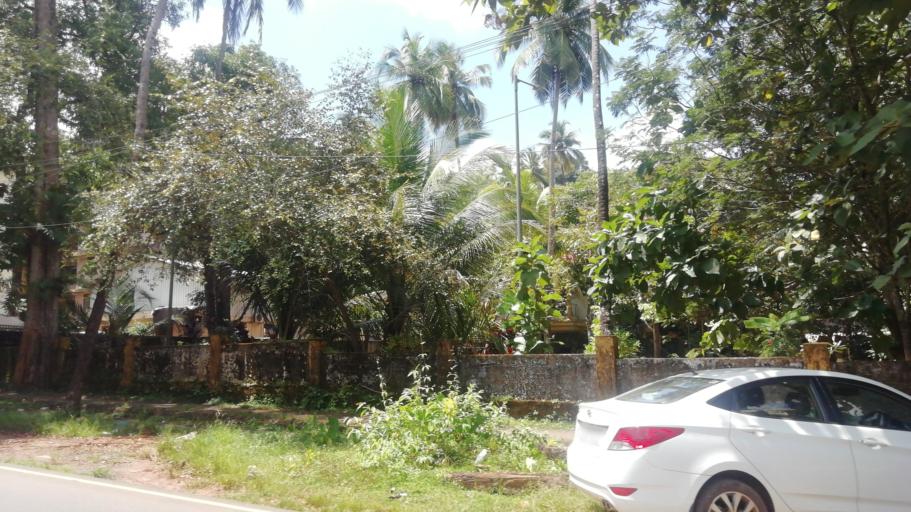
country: IN
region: Goa
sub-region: North Goa
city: Ponda
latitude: 15.3906
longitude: 74.0035
